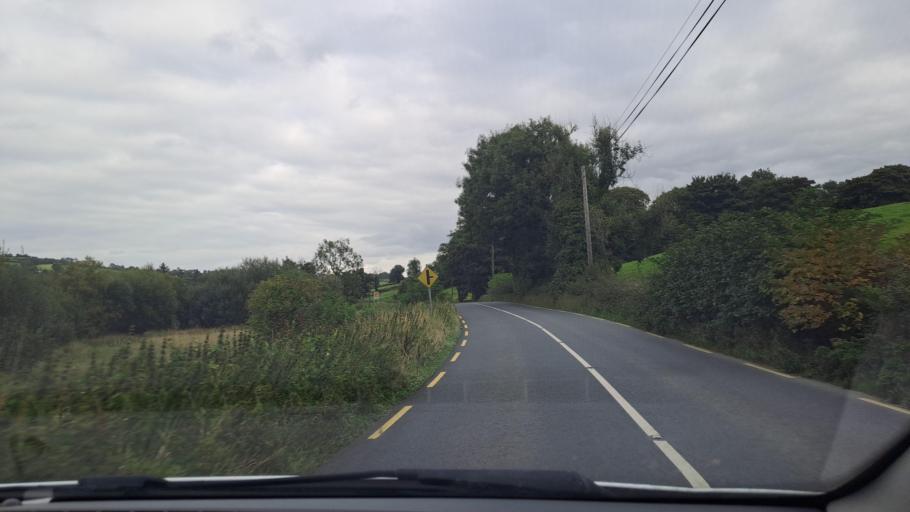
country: IE
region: Ulster
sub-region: An Cabhan
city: Kingscourt
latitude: 53.9955
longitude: -6.8421
